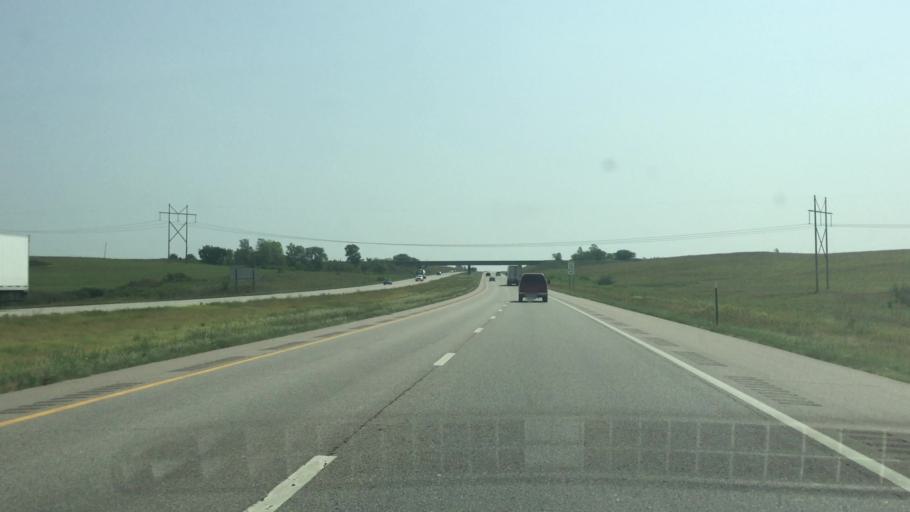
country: US
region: Kansas
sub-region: Lyon County
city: Emporia
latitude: 38.4102
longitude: -96.0854
